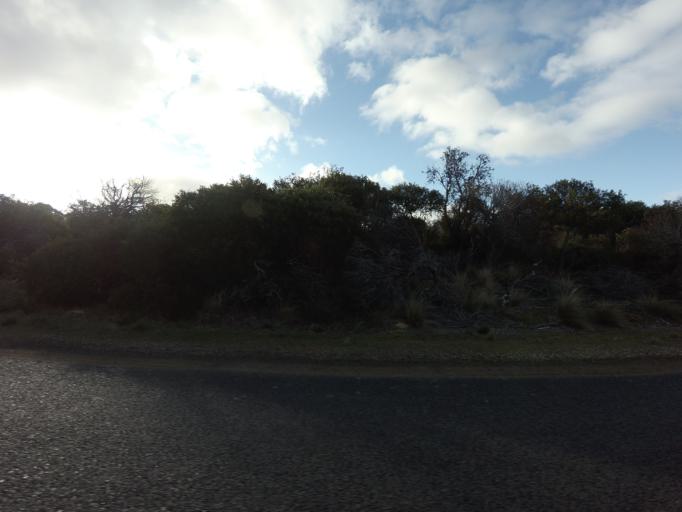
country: AU
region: Tasmania
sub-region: Break O'Day
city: St Helens
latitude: -42.0897
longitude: 148.1334
